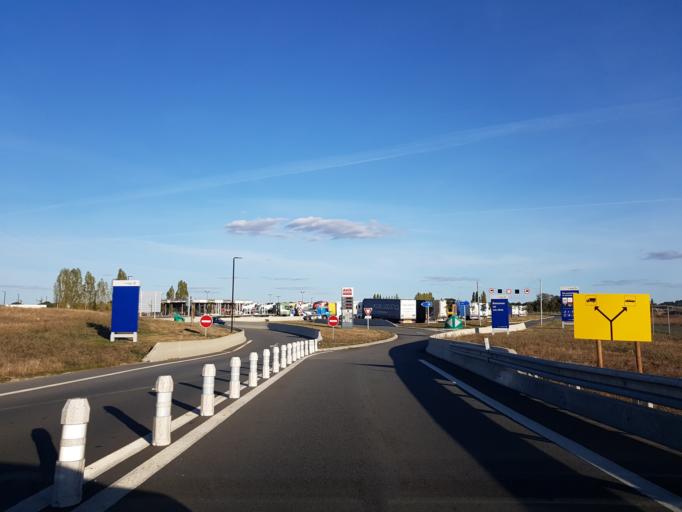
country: FR
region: Pays de la Loire
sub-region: Departement de la Mayenne
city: Bonchamp-les-Laval
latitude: 48.0953
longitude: -0.6975
